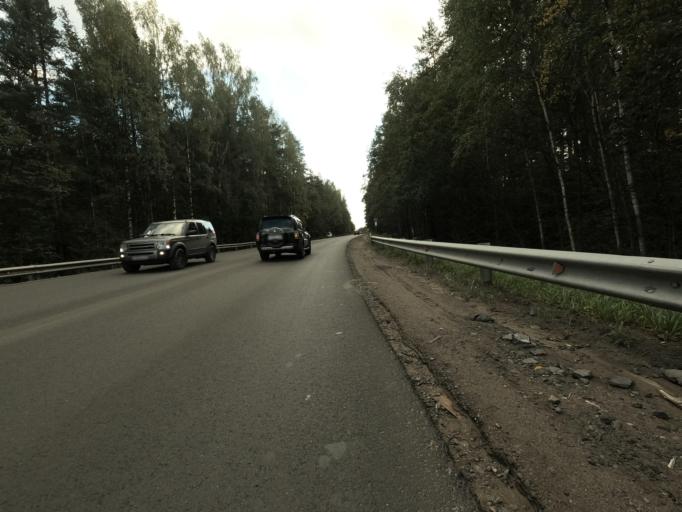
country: RU
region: Leningrad
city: Koltushi
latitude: 59.9579
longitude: 30.6592
